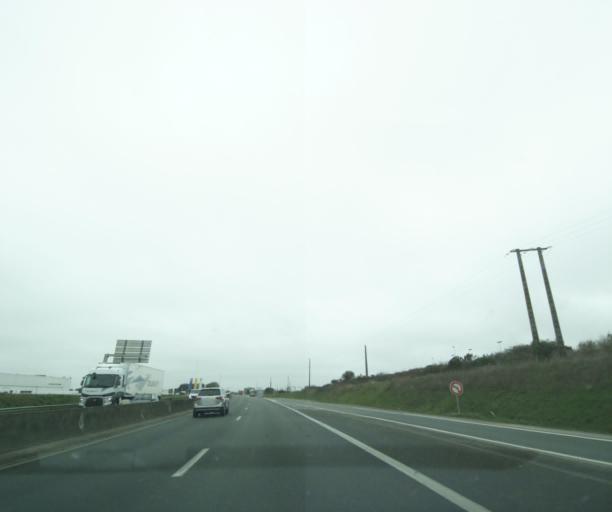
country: FR
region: Poitou-Charentes
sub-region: Departement de la Charente-Maritime
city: Perigny
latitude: 46.1554
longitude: -1.1155
